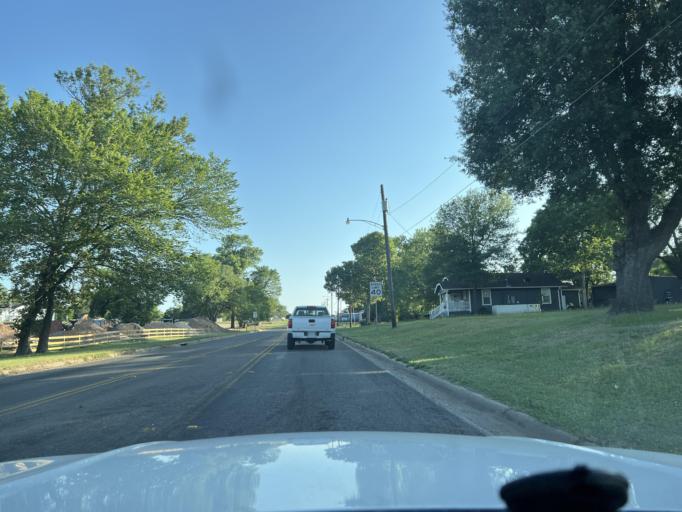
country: US
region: Texas
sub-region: Washington County
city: Brenham
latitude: 30.1773
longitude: -96.3858
